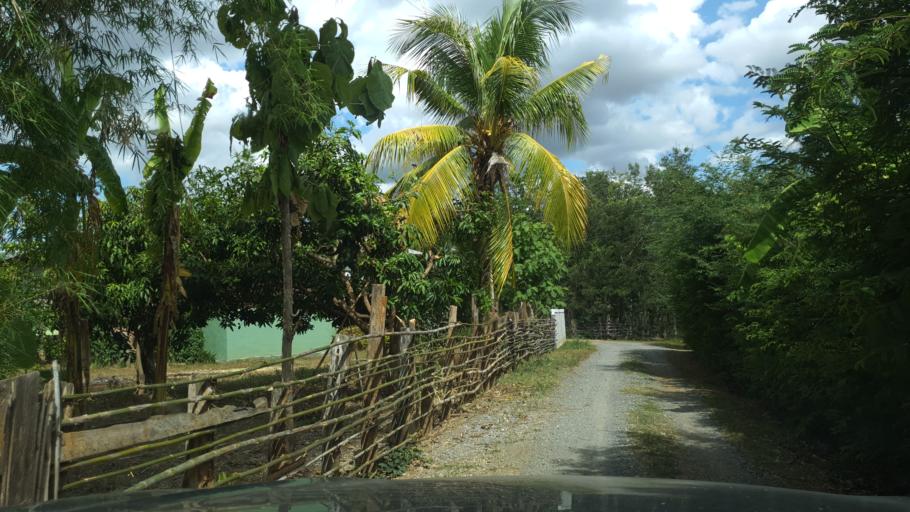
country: TH
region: Sukhothai
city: Thung Saliam
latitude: 17.3256
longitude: 99.5480
